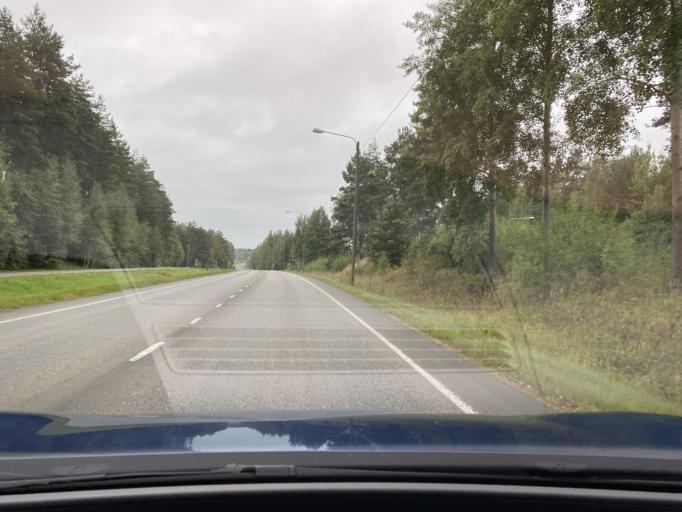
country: FI
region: Kymenlaakso
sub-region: Kouvola
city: Kouvola
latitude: 60.8960
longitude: 26.6041
